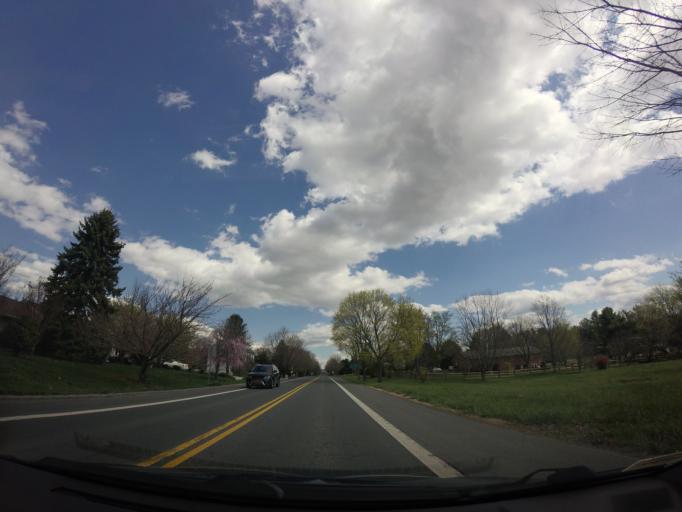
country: US
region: West Virginia
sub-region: Jefferson County
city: Shepherdstown
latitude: 39.4541
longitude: -77.7638
